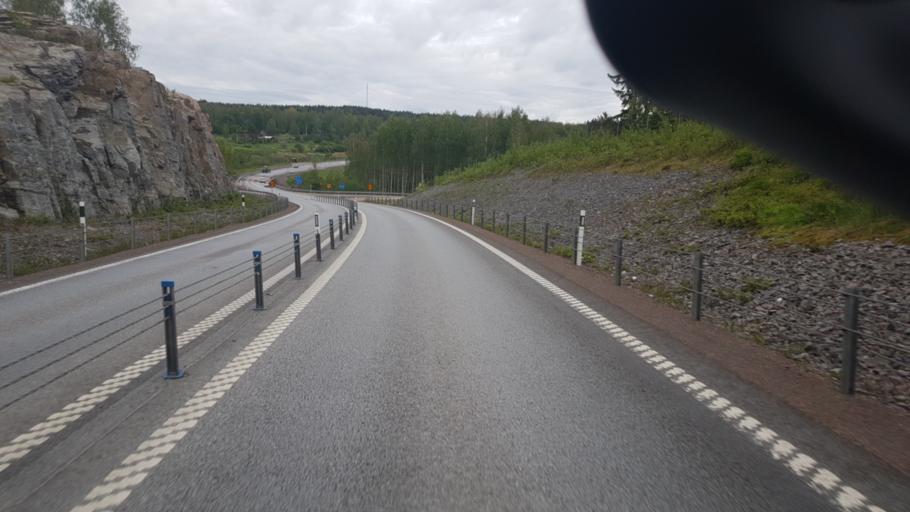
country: SE
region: Vaermland
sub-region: Eda Kommun
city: Amotfors
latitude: 59.7570
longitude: 12.4356
